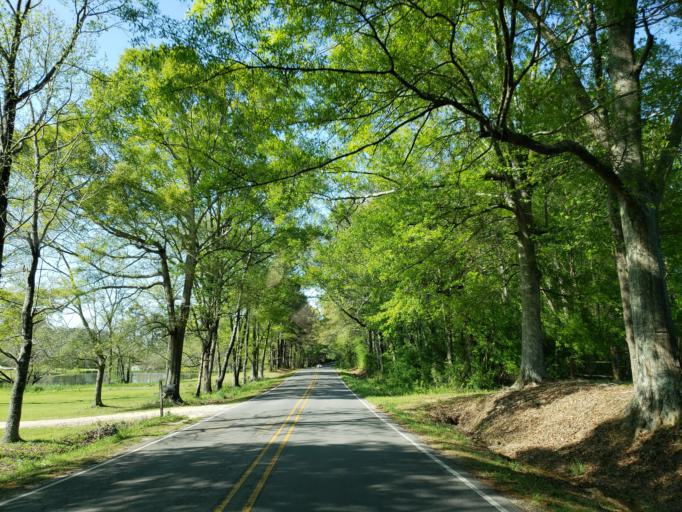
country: US
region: Mississippi
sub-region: Forrest County
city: Rawls Springs
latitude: 31.5050
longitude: -89.3600
